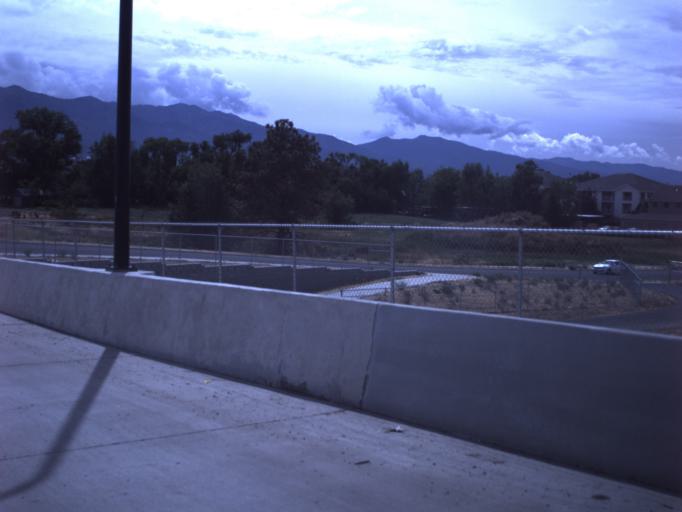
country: US
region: Utah
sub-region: Davis County
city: Clearfield
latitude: 41.1036
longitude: -112.0194
